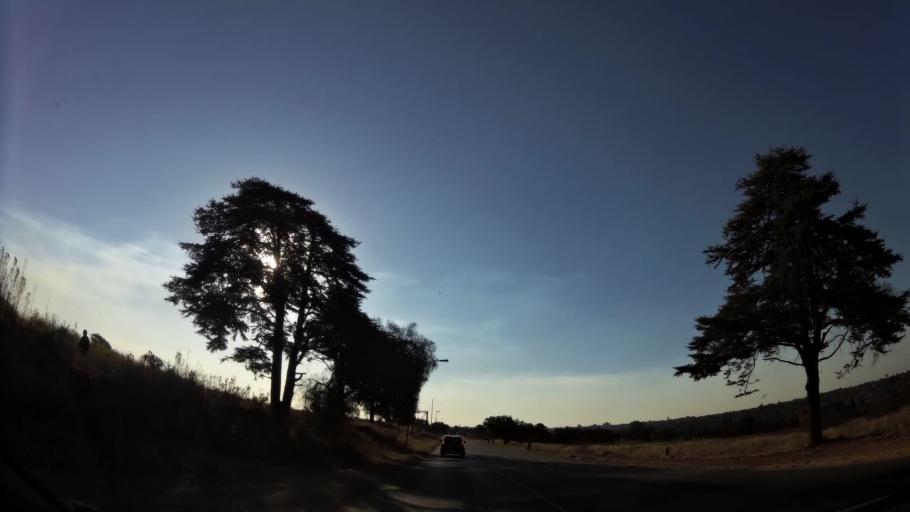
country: ZA
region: Gauteng
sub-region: City of Johannesburg Metropolitan Municipality
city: Roodepoort
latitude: -26.1693
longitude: 27.8728
